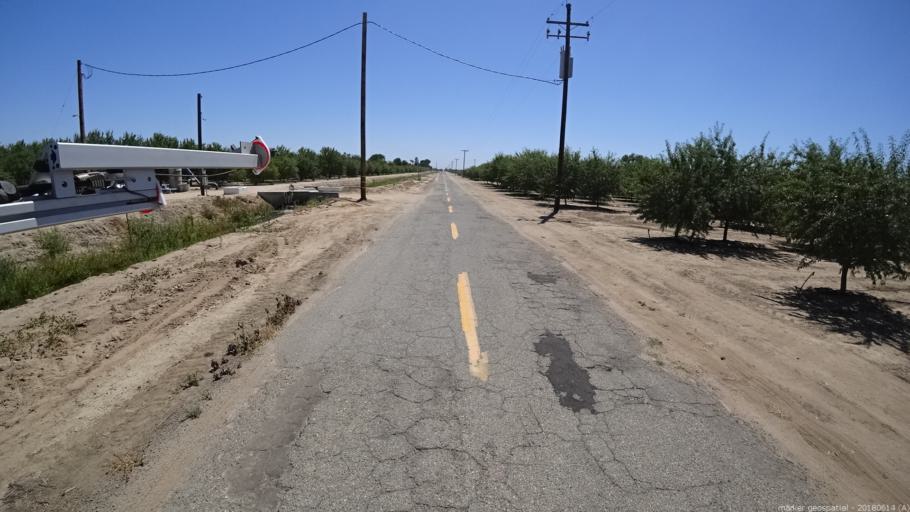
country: US
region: California
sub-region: Madera County
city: Fairmead
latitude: 36.9892
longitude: -120.2409
